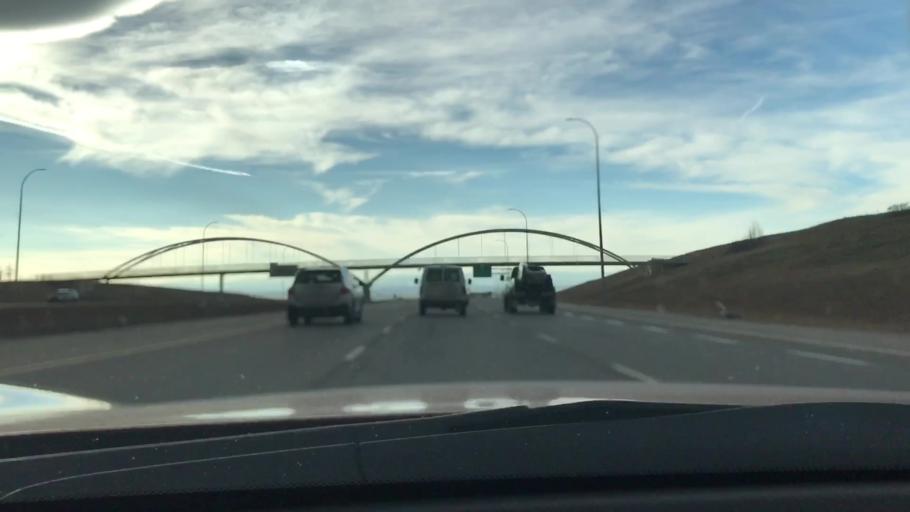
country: CA
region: Alberta
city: Calgary
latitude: 51.1395
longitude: -114.2113
